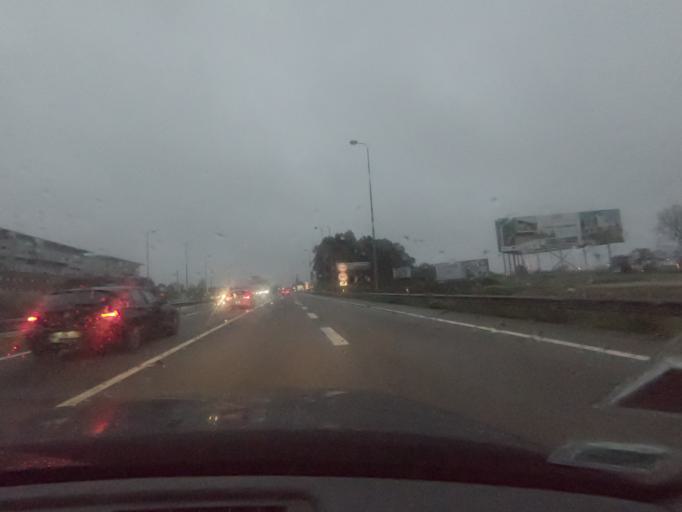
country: PT
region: Porto
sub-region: Matosinhos
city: Santa Cruz do Bispo
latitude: 41.2307
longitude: -8.6956
